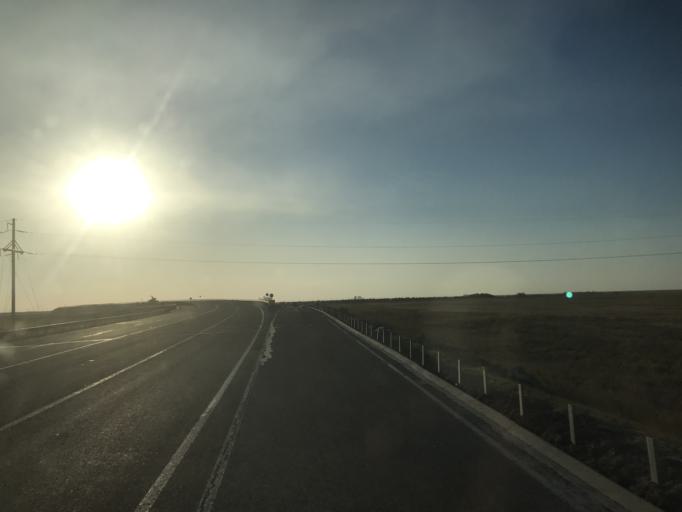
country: KZ
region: Pavlodar
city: Leninskiy
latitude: 52.1558
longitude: 76.8288
